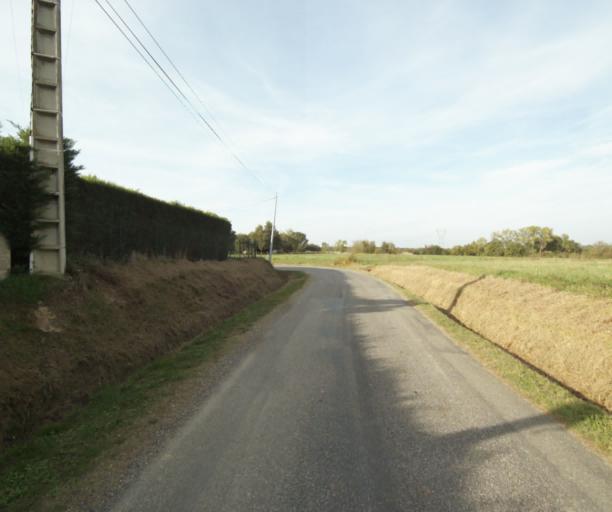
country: FR
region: Midi-Pyrenees
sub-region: Departement du Tarn-et-Garonne
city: Campsas
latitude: 43.9028
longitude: 1.3231
